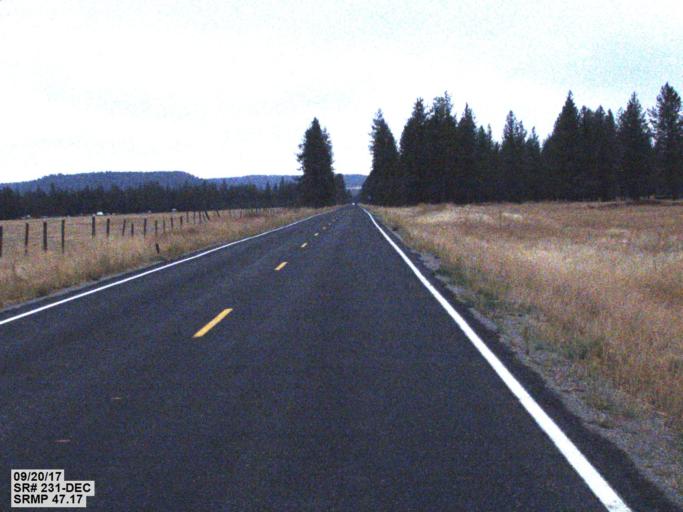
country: US
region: Washington
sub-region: Spokane County
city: Fairchild Air Force Base
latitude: 47.8708
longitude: -117.8397
